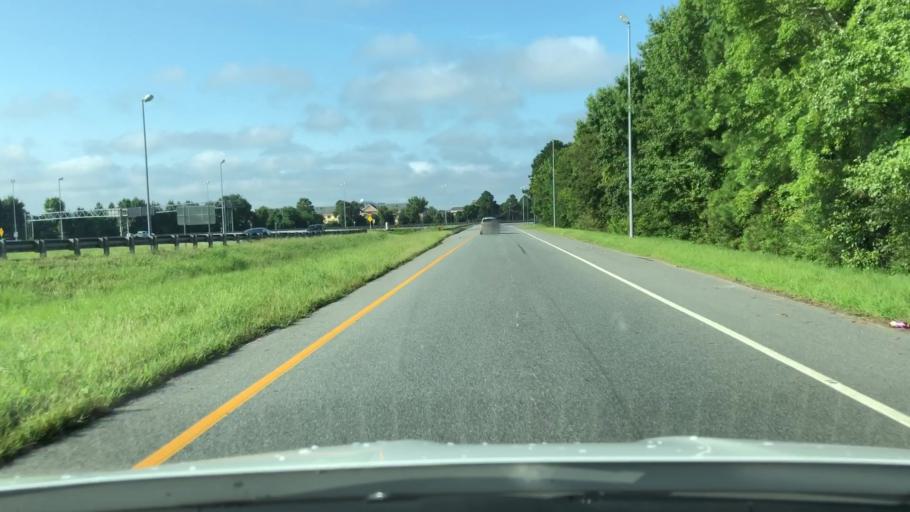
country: US
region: Virginia
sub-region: City of Chesapeake
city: Chesapeake
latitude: 36.7853
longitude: -76.2363
